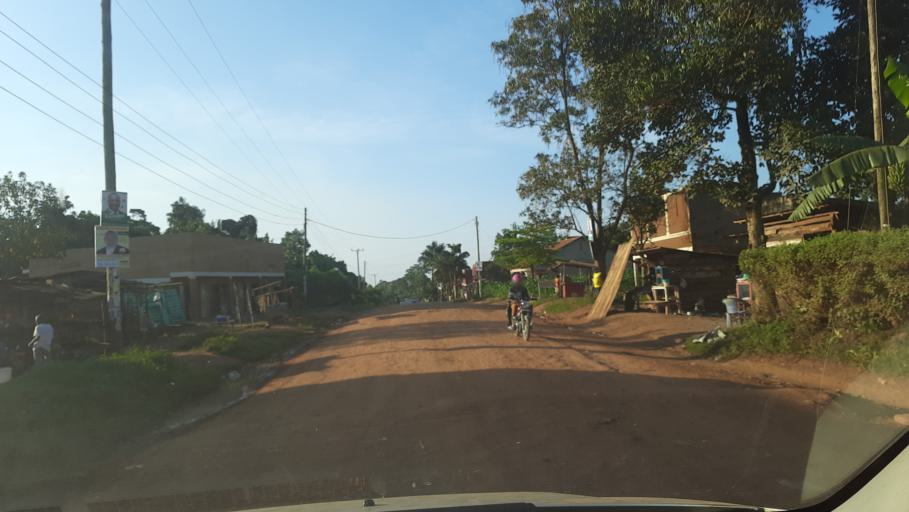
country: UG
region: Central Region
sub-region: Mukono District
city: Mukono
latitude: 0.3736
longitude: 32.7478
